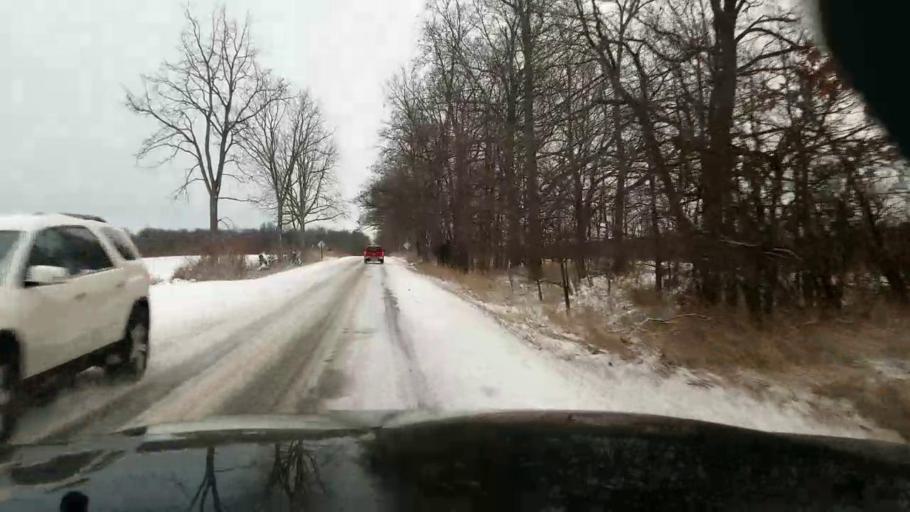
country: US
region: Michigan
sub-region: Jackson County
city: Spring Arbor
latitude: 42.1445
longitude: -84.4990
